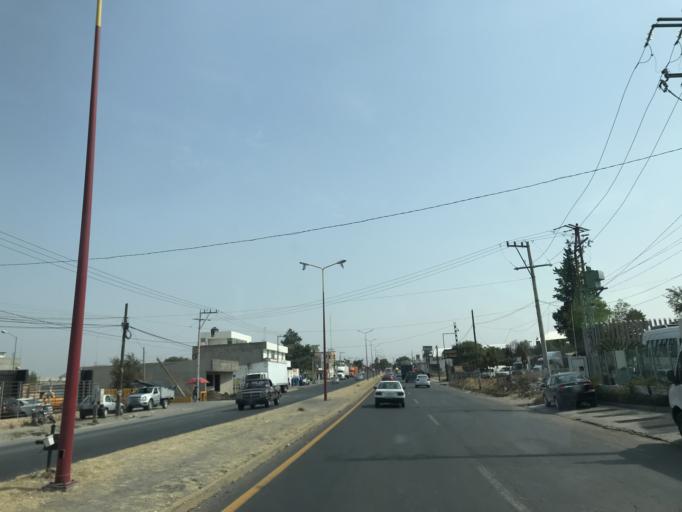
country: MX
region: Tlaxcala
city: Xiloxoxtla
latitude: 19.2661
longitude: -98.1987
